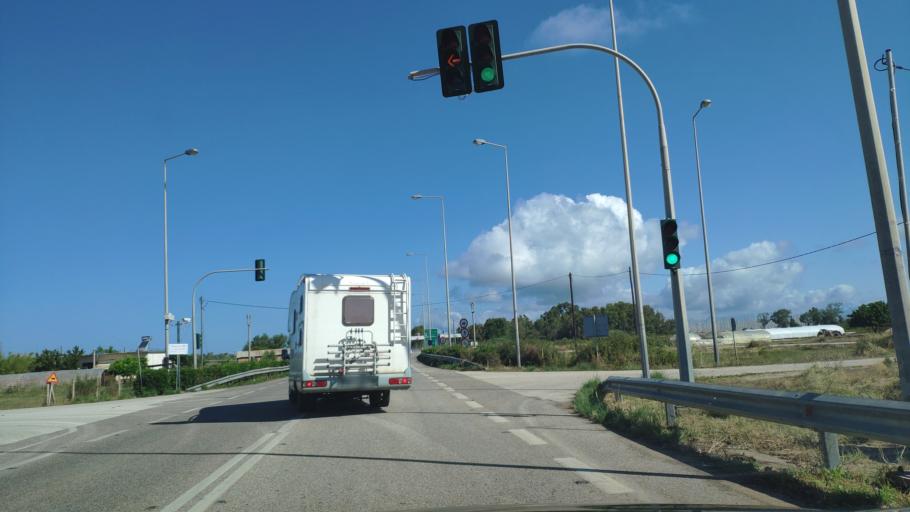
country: GR
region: Epirus
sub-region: Nomos Prevezis
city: Preveza
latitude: 38.9375
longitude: 20.7681
